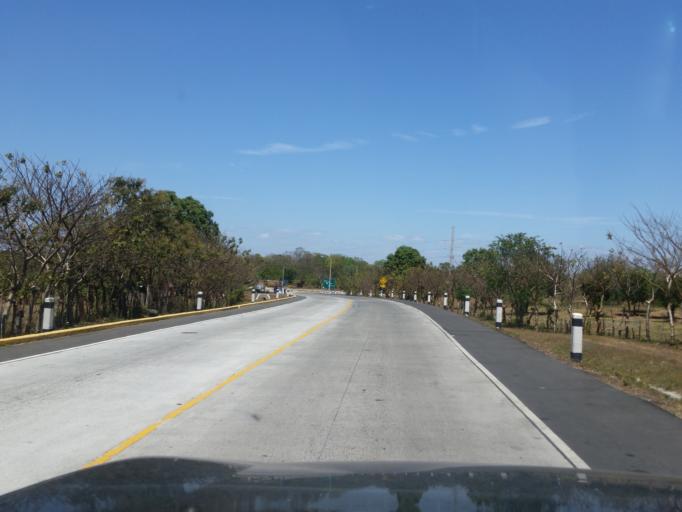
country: NI
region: Masaya
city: Masaya
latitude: 11.9774
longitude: -86.0728
